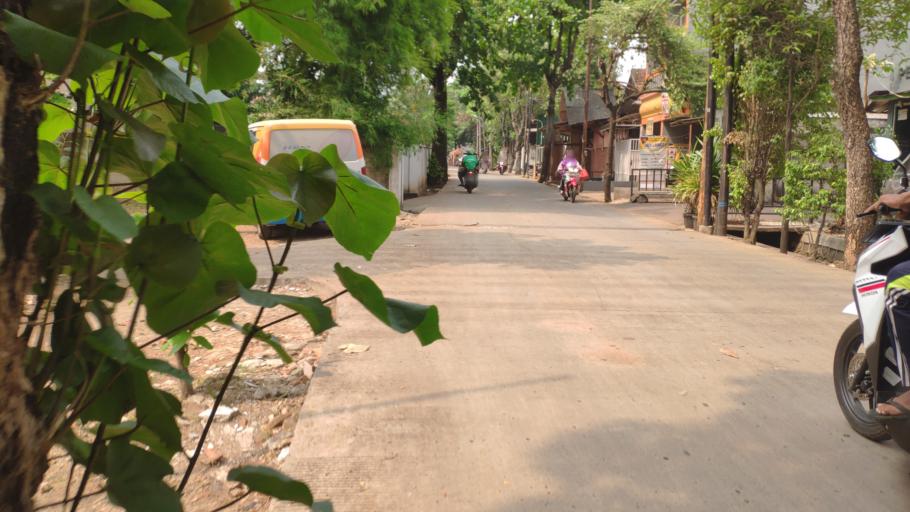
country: ID
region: West Java
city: Depok
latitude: -6.3425
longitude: 106.8126
